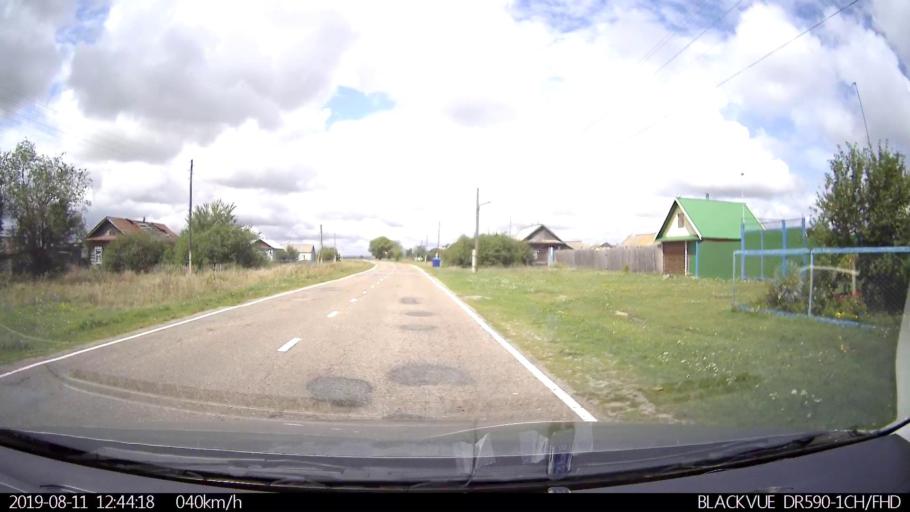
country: RU
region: Ulyanovsk
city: Ignatovka
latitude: 53.8542
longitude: 47.7372
